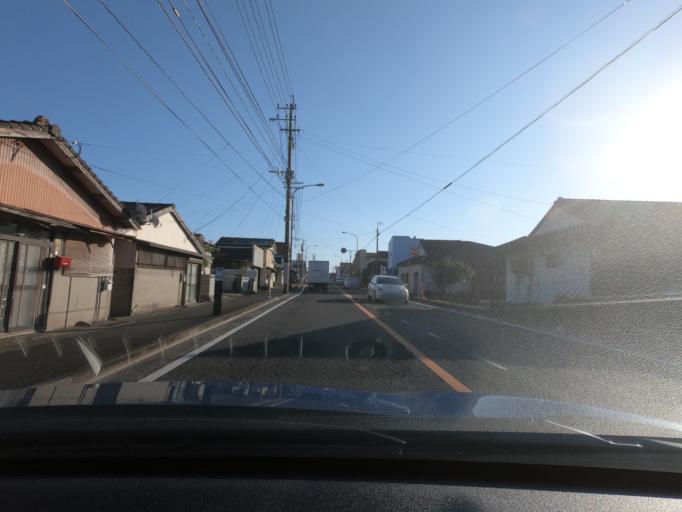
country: JP
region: Kagoshima
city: Akune
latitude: 32.0243
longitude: 130.1957
